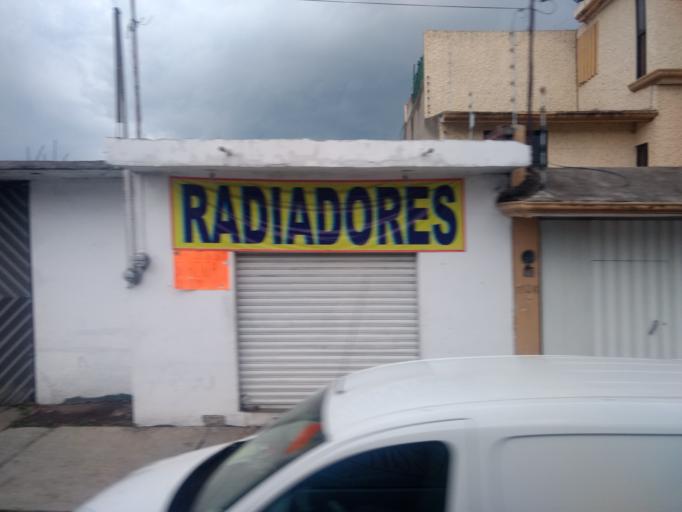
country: MX
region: Tlaxcala
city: Apizaco
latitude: 19.4150
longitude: -98.1483
